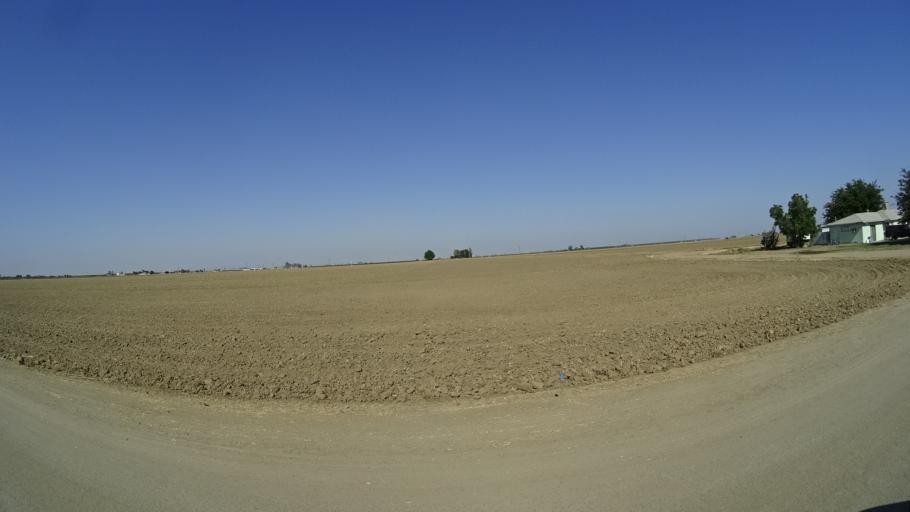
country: US
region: California
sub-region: Kings County
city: Home Garden
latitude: 36.2359
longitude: -119.5741
